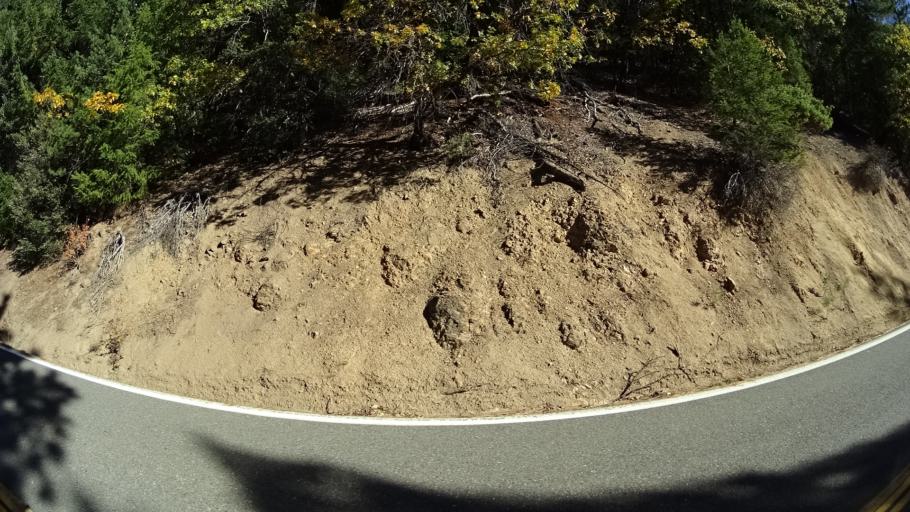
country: US
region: California
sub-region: Trinity County
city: Weaverville
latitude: 41.2124
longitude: -123.0311
